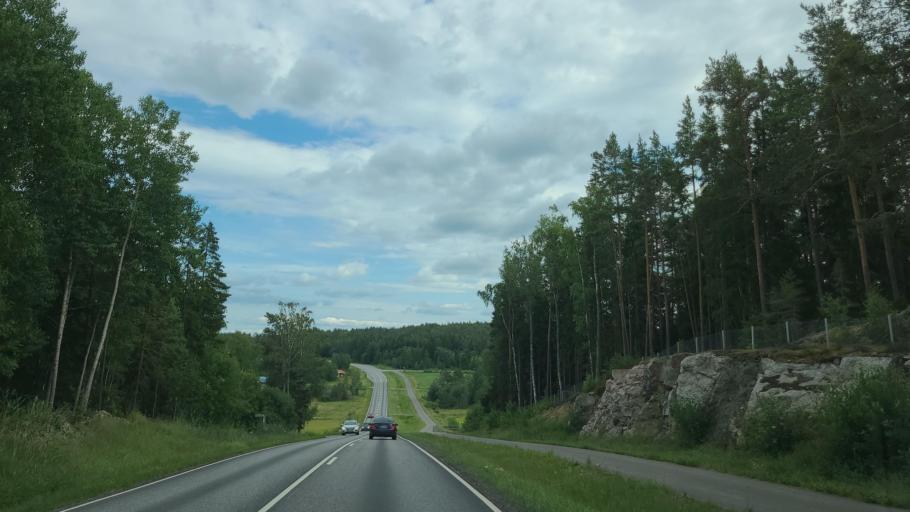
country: FI
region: Varsinais-Suomi
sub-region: Turku
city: Rymaettylae
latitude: 60.3951
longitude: 21.9015
